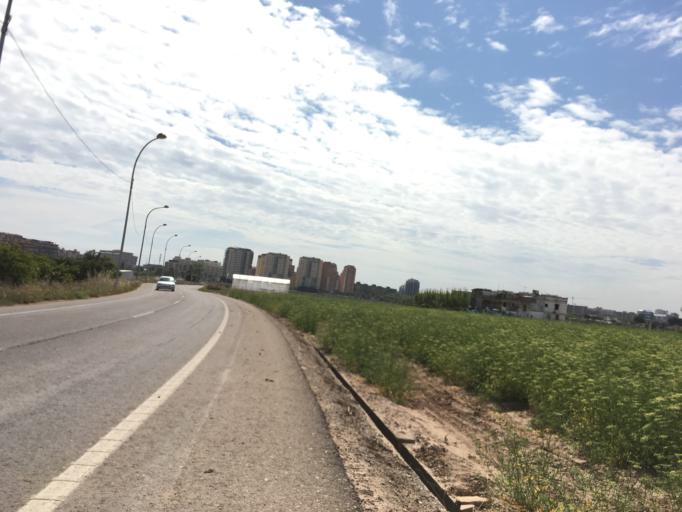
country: ES
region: Valencia
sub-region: Provincia de Valencia
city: Mislata
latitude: 39.4896
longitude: -0.4132
